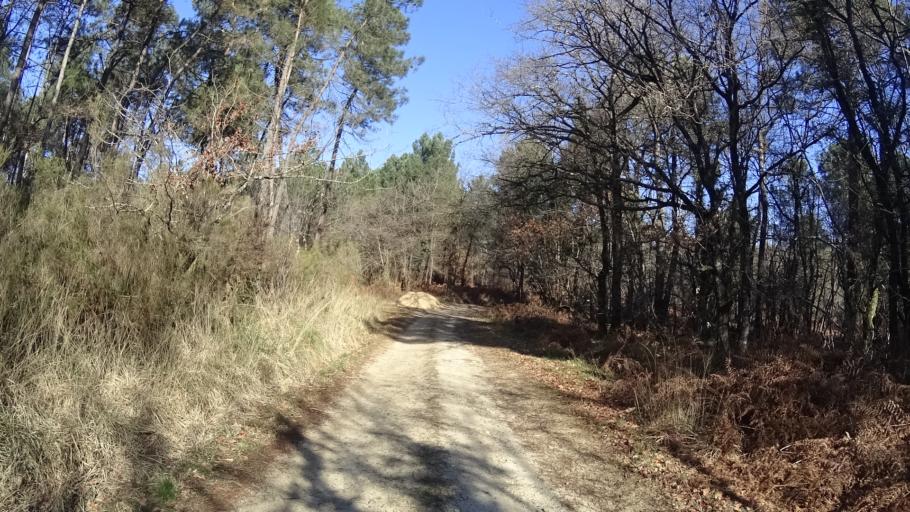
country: FR
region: Aquitaine
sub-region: Departement de la Dordogne
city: Montpon-Menesterol
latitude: 45.0483
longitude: 0.2434
